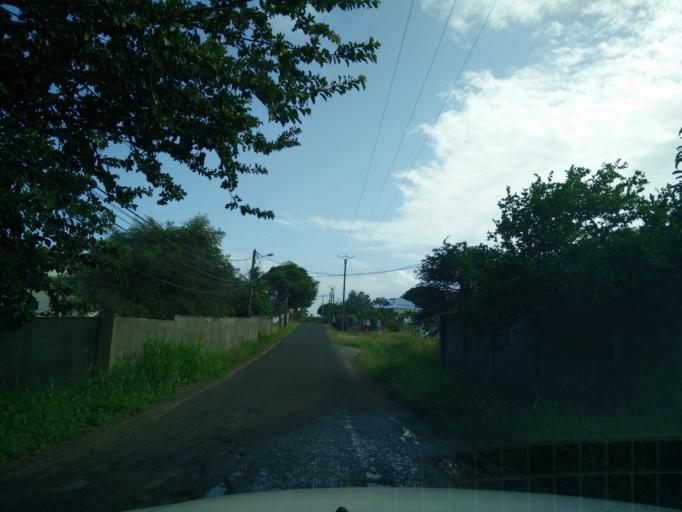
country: GP
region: Guadeloupe
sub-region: Guadeloupe
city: Sainte-Anne
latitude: 16.2465
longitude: -61.3806
